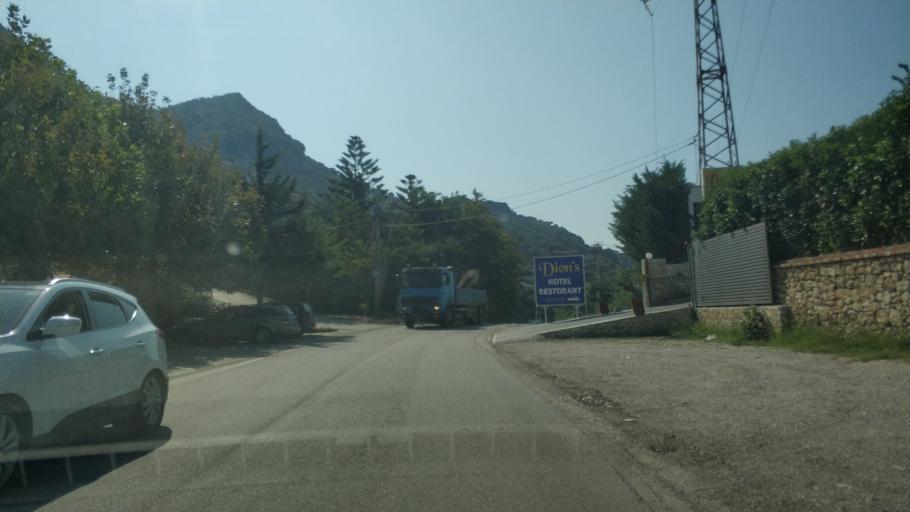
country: AL
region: Vlore
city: Vlore
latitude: 40.4033
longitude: 19.4803
